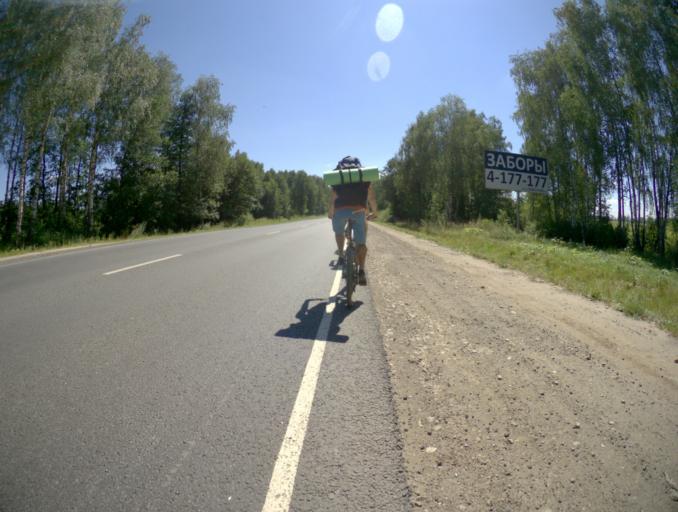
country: RU
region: Nizjnij Novgorod
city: Neklyudovo
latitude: 56.4265
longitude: 43.9911
